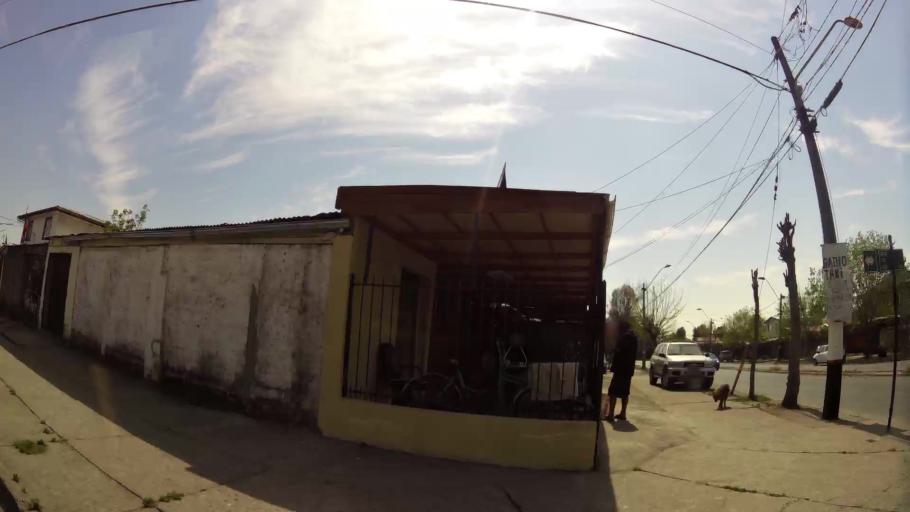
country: CL
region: Santiago Metropolitan
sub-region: Provincia de Santiago
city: La Pintana
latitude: -33.5558
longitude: -70.6554
